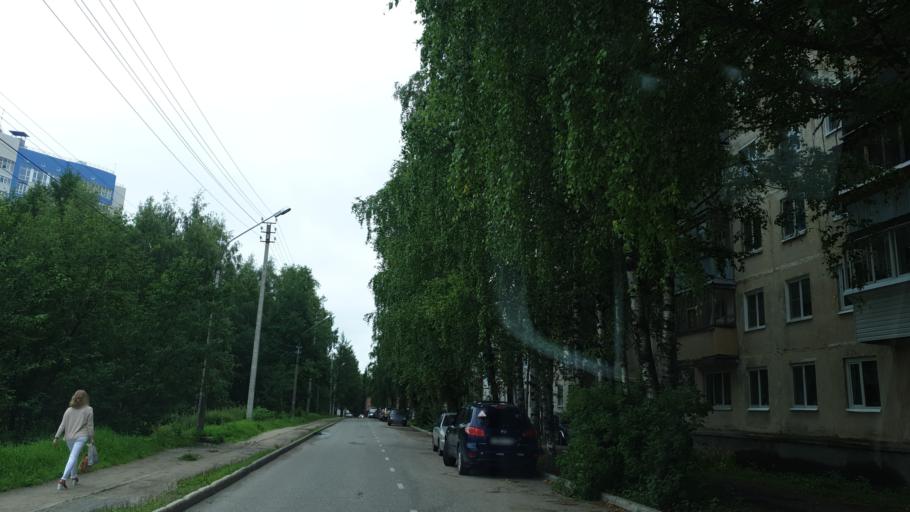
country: RU
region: Komi Republic
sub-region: Syktyvdinskiy Rayon
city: Syktyvkar
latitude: 61.6621
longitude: 50.8242
